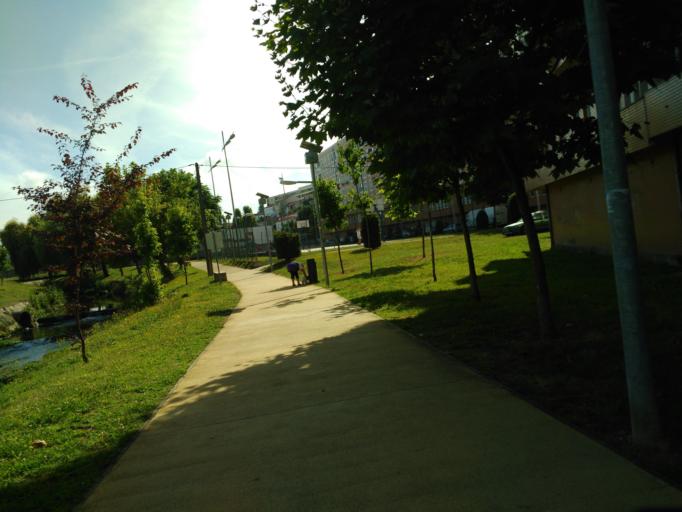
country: PT
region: Braga
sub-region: Braga
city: Braga
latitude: 41.5377
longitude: -8.4321
